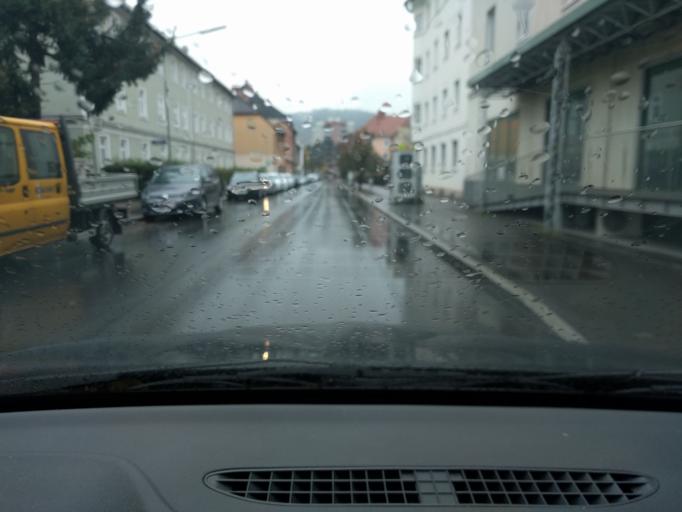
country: AT
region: Styria
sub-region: Politischer Bezirk Leoben
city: Leoben
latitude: 47.3848
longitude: 15.1012
